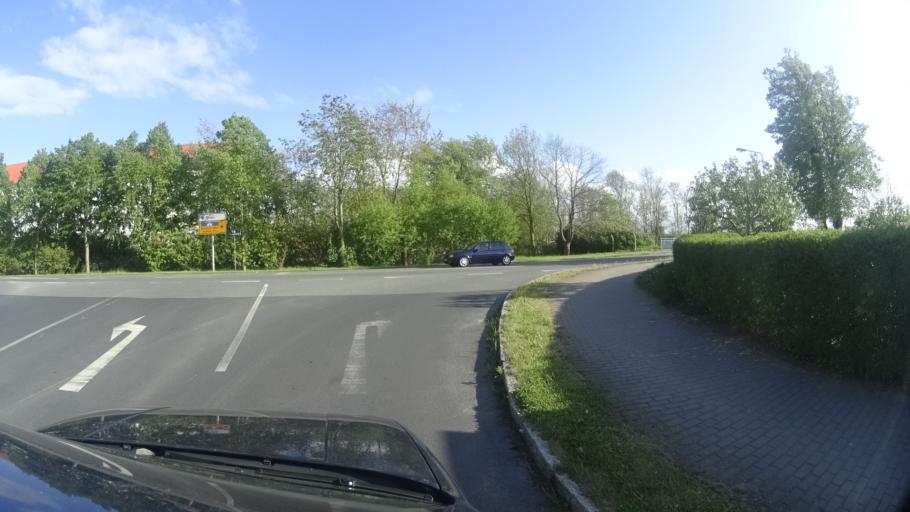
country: DE
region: Mecklenburg-Vorpommern
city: Ribnitz-Damgarten
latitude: 54.2406
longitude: 12.4110
